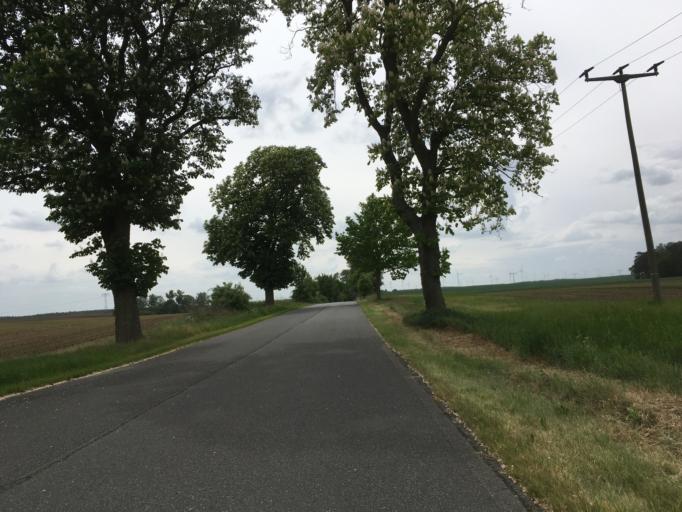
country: DE
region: Brandenburg
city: Melchow
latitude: 52.7297
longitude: 13.7522
